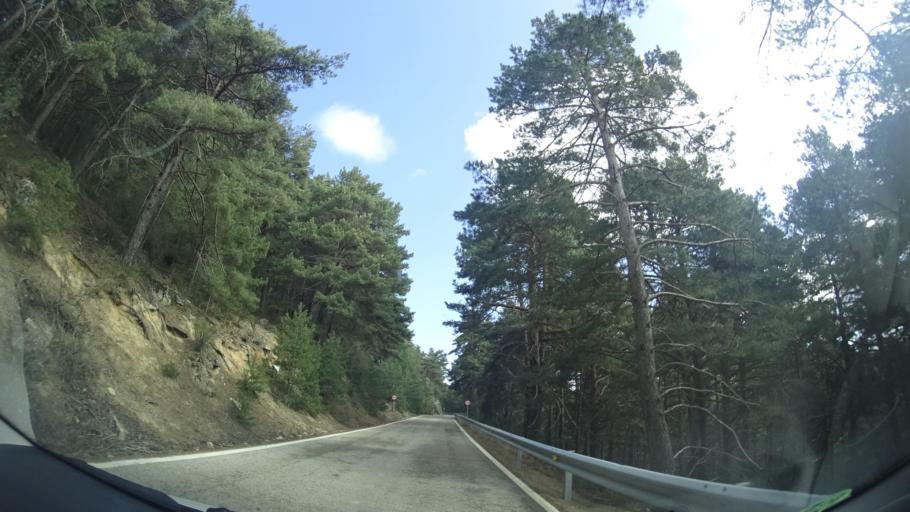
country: ES
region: Madrid
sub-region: Provincia de Madrid
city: Miraflores de la Sierra
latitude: 40.8608
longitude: -3.7645
